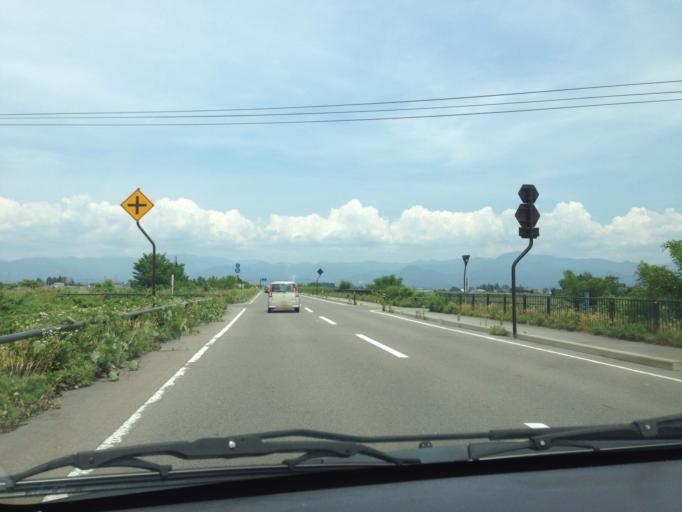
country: JP
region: Fukushima
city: Kitakata
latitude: 37.6069
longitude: 139.8484
